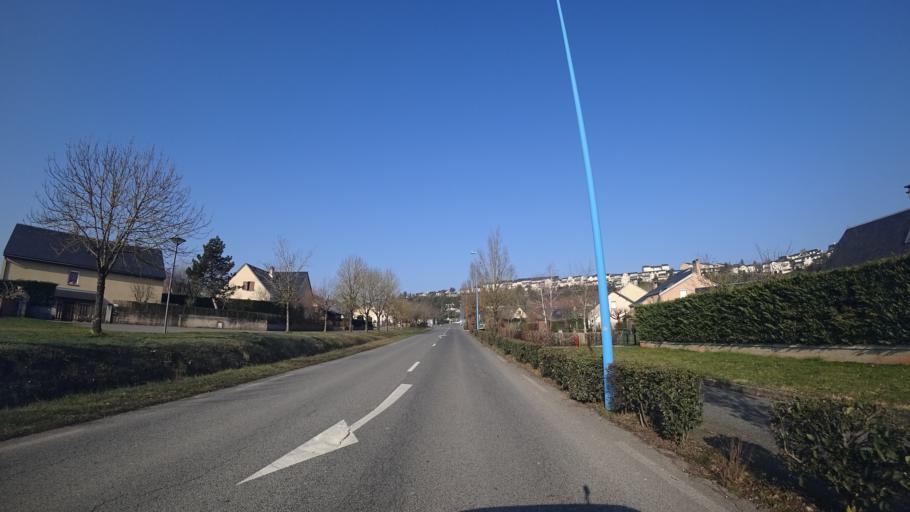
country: FR
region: Midi-Pyrenees
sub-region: Departement de l'Aveyron
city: Rodez
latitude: 44.3734
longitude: 2.5757
